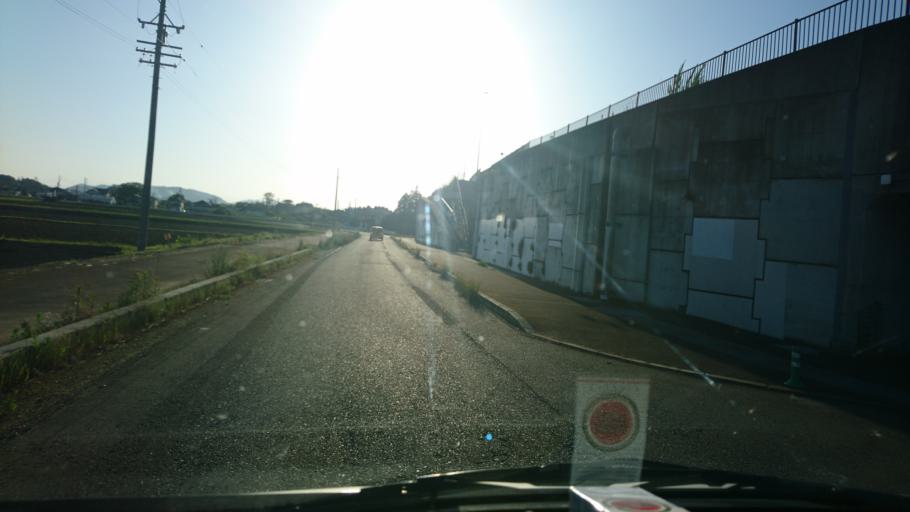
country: JP
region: Gifu
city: Mitake
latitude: 35.4301
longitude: 137.0835
